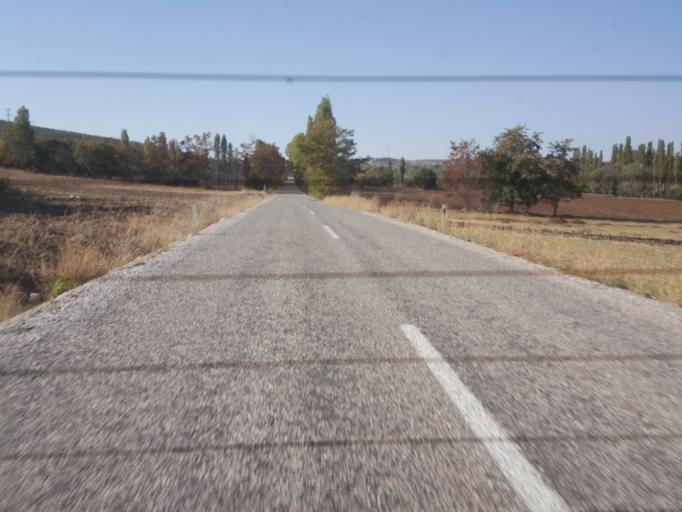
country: TR
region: Corum
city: Seydim
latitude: 40.5579
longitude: 34.7597
